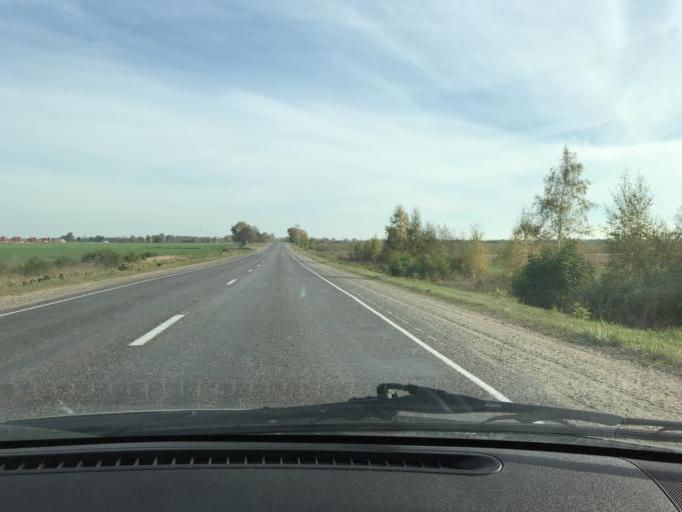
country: BY
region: Brest
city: Asnyezhytsy
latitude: 52.2079
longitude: 26.0521
